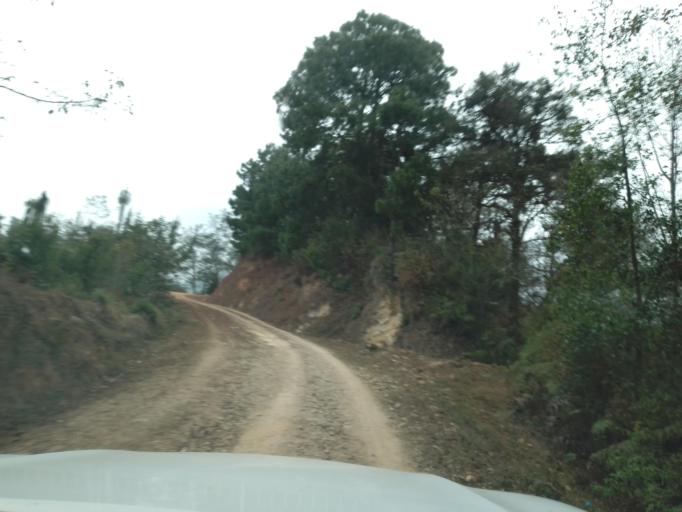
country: GT
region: San Marcos
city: Tacana
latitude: 15.2192
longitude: -92.2163
